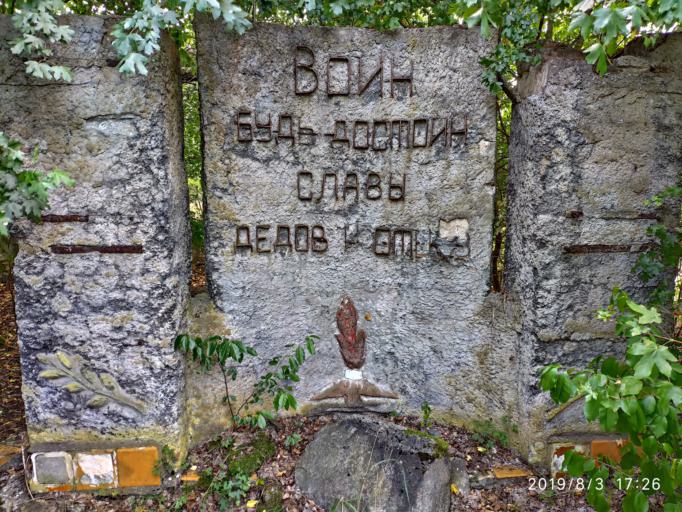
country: PL
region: Lubusz
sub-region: Powiat zaganski
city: Szprotawa
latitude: 51.4457
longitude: 15.5650
